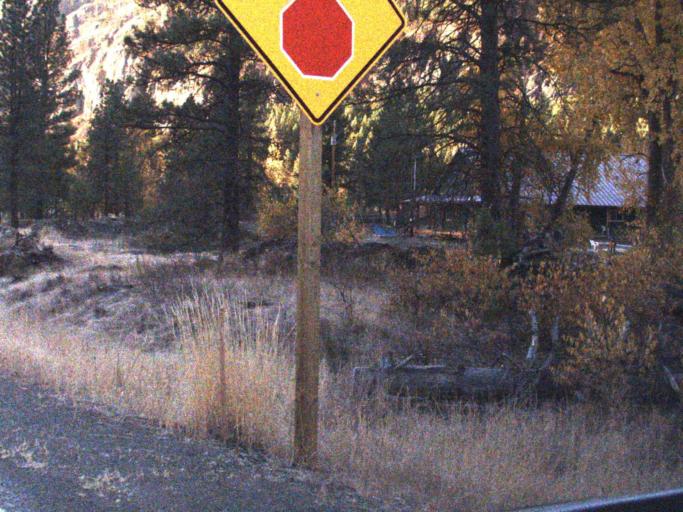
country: US
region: Washington
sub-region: Ferry County
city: Republic
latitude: 48.4607
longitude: -118.7514
